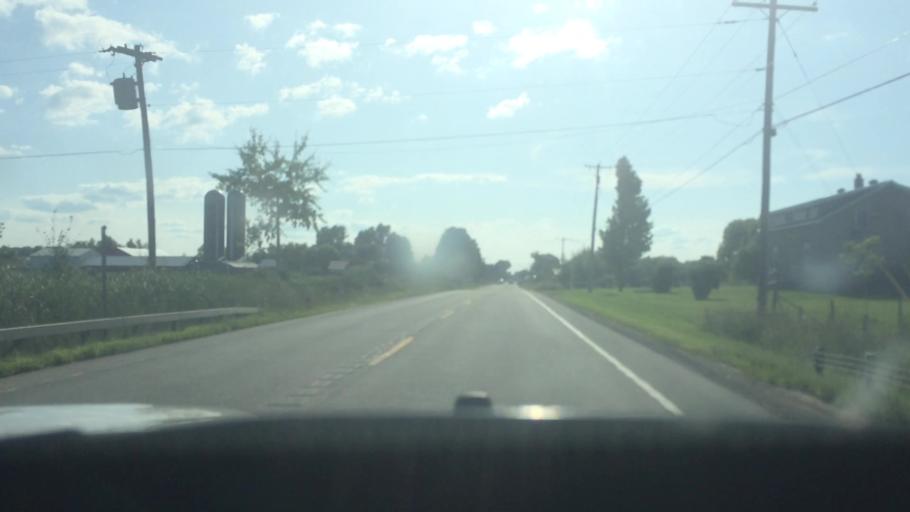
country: US
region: New York
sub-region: Franklin County
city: Malone
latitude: 44.8084
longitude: -74.4143
